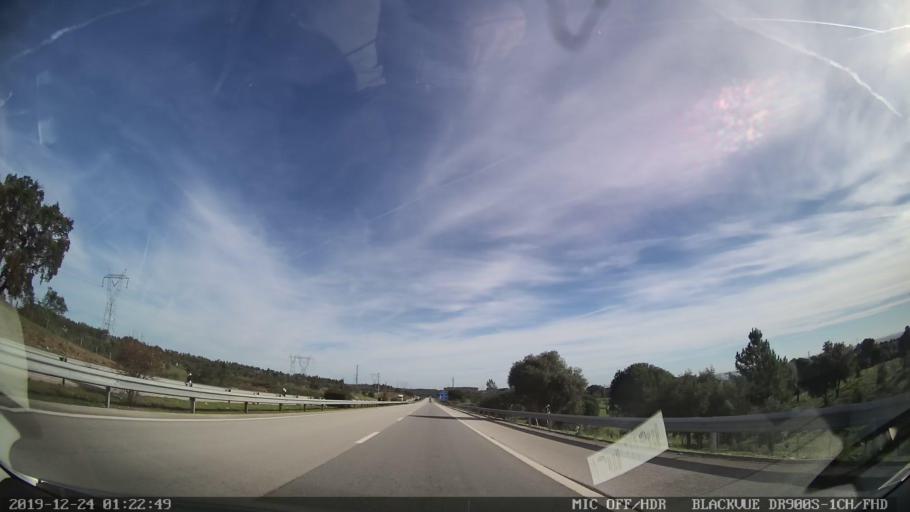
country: PT
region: Santarem
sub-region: Abrantes
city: Abrantes
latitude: 39.4938
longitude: -8.1998
